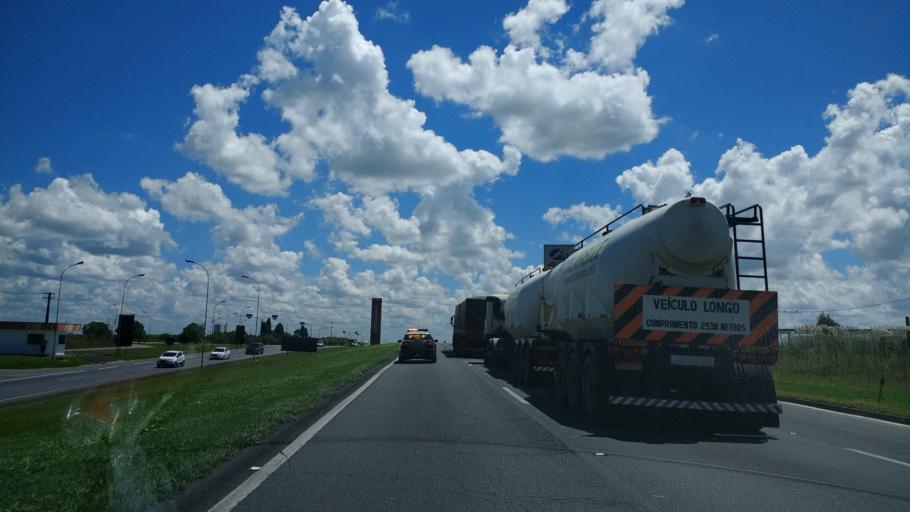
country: BR
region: Parana
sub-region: Campo Largo
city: Campo Largo
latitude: -25.4728
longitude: -49.6989
